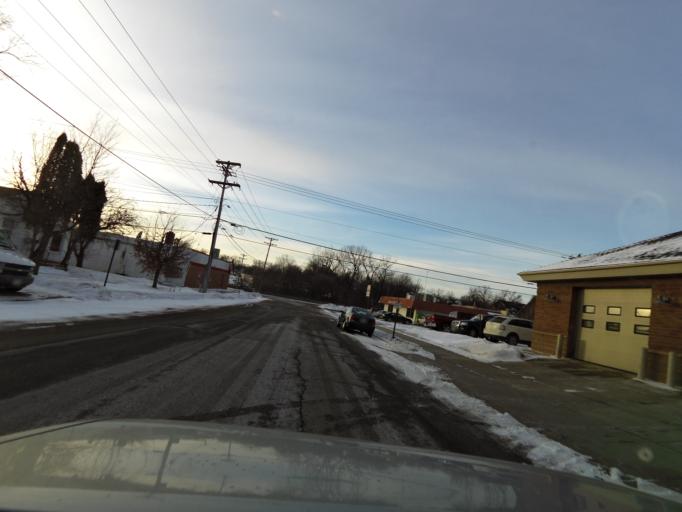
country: US
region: Wisconsin
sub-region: Pierce County
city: River Falls
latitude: 44.8614
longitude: -92.6232
